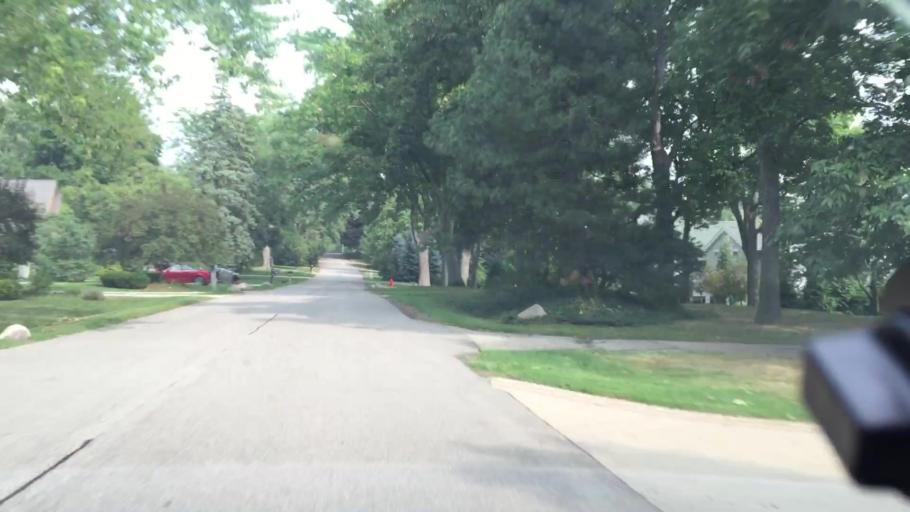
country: US
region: Michigan
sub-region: Oakland County
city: Sylvan Lake
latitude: 42.5959
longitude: -83.2900
